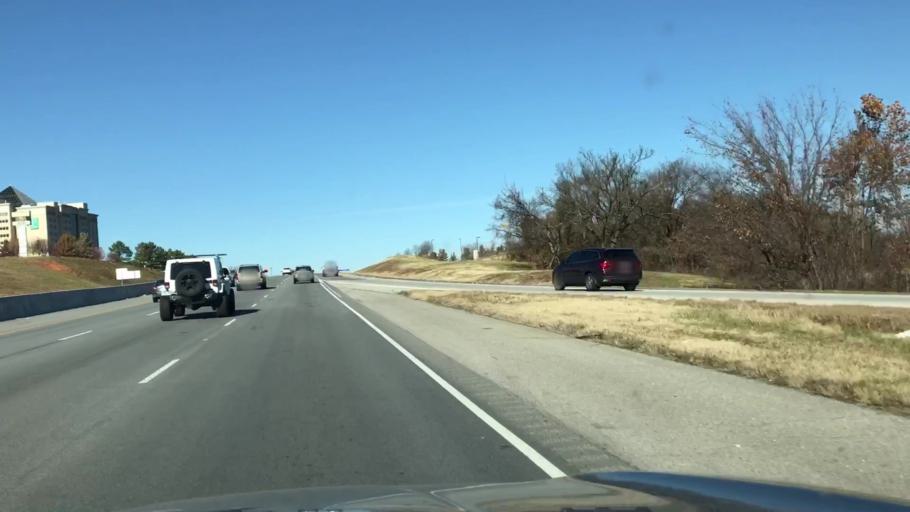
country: US
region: Arkansas
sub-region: Benton County
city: Cave Springs
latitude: 36.3033
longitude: -94.1819
